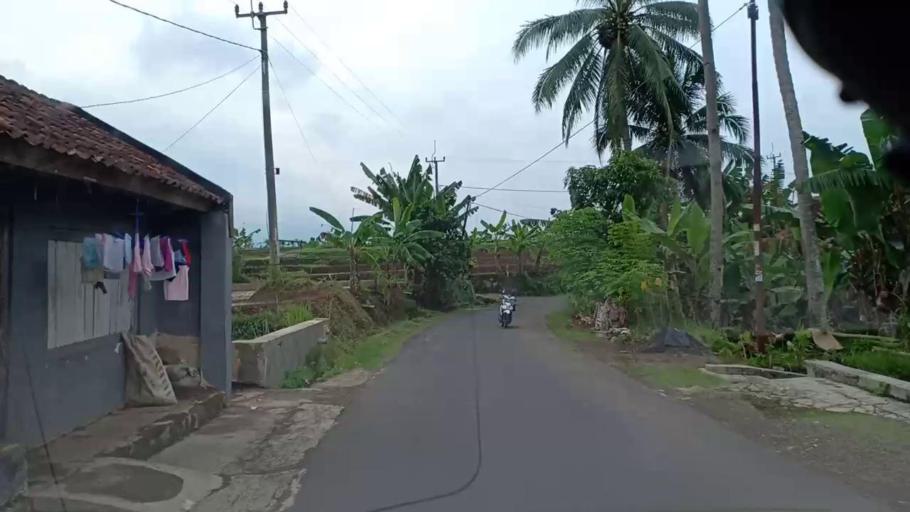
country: ID
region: West Java
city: Kertasari
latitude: -7.3387
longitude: 108.2763
